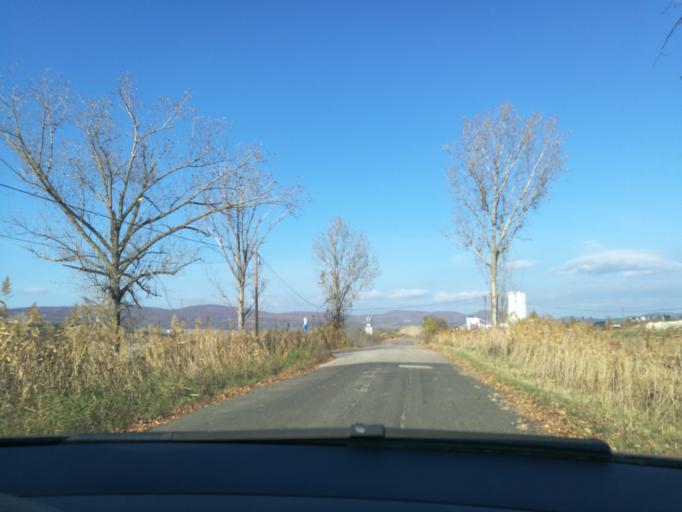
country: HU
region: Nograd
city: Paszto
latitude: 47.9058
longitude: 19.6868
